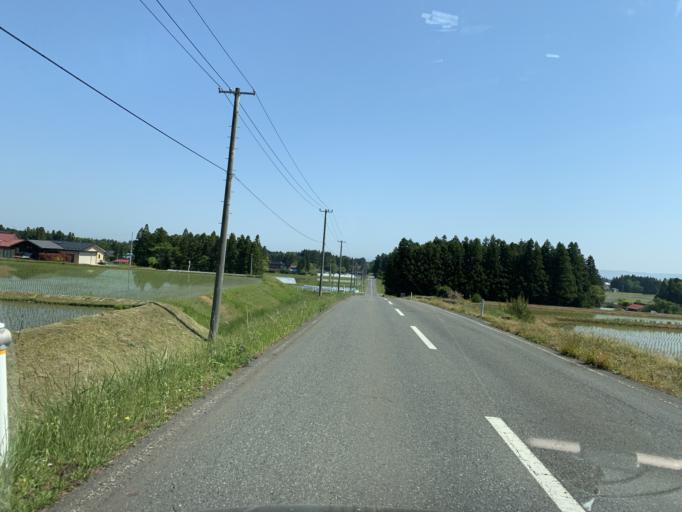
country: JP
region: Iwate
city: Mizusawa
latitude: 39.0810
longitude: 141.0655
